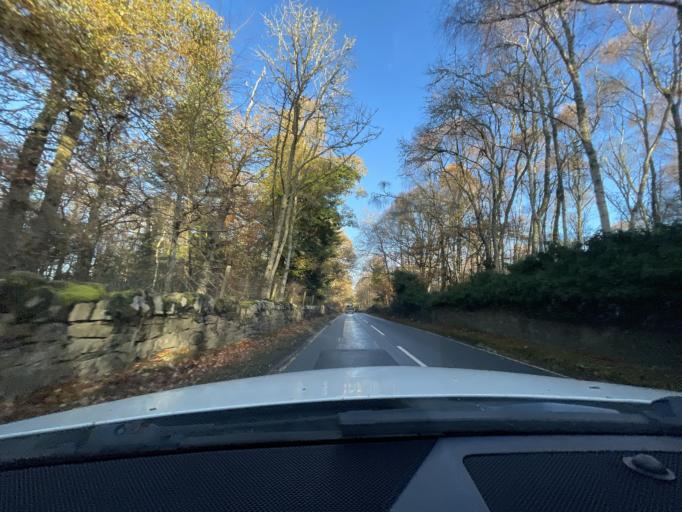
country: GB
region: Scotland
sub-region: Highland
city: Inverness
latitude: 57.4430
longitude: -4.2612
